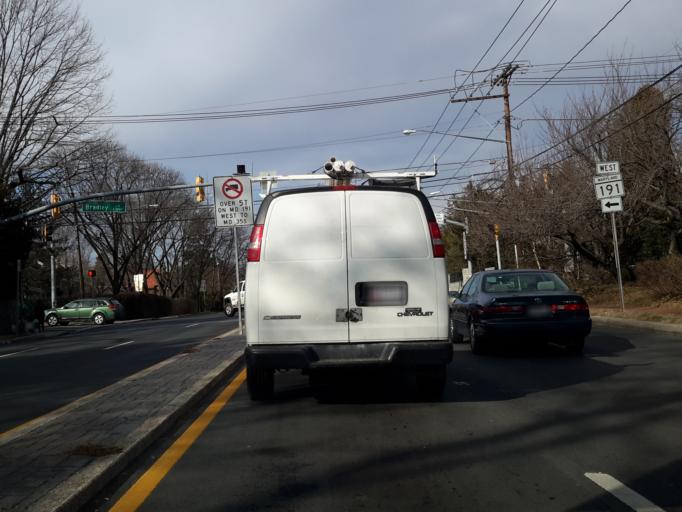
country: US
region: Maryland
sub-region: Montgomery County
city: Chevy Chase
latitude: 38.9762
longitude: -77.0771
